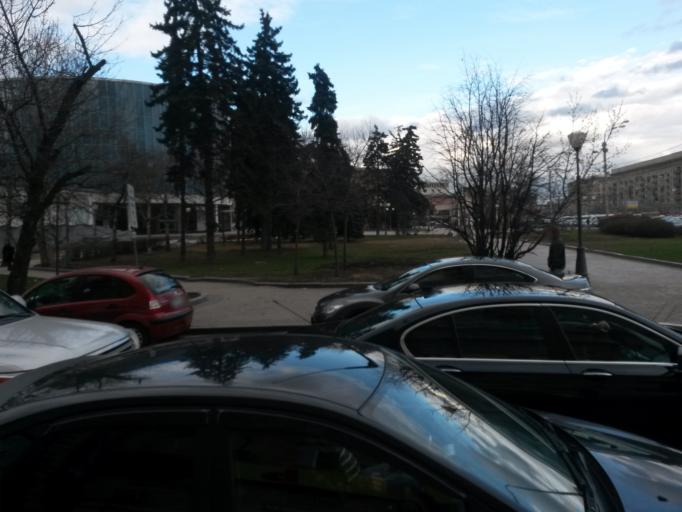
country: RU
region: Moscow
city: Vorob'yovo
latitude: 55.7379
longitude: 37.5221
